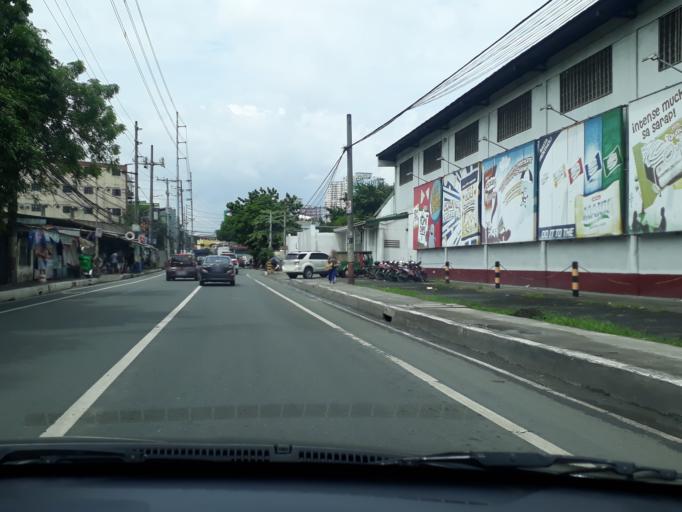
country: PH
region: Metro Manila
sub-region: Pasig
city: Pasig City
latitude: 14.5927
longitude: 121.0870
